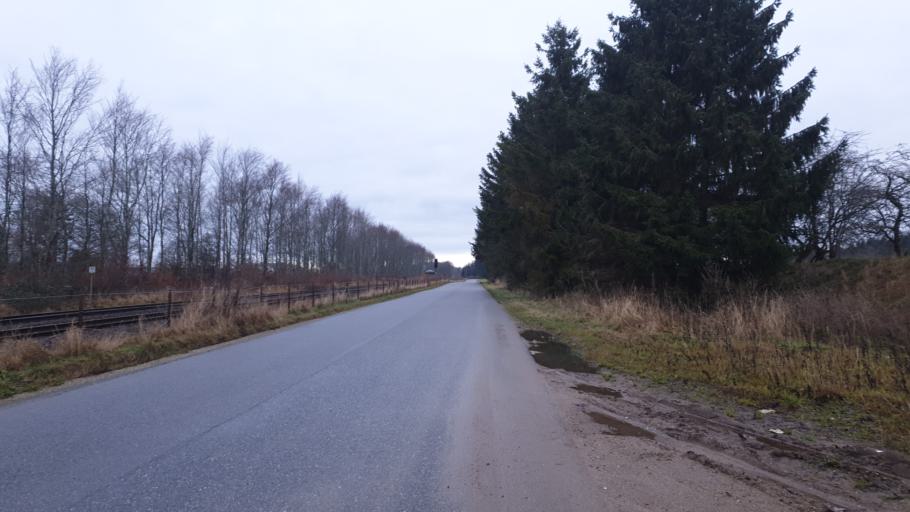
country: DK
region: Central Jutland
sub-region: Hedensted Kommune
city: Hedensted
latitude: 55.7911
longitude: 9.7005
